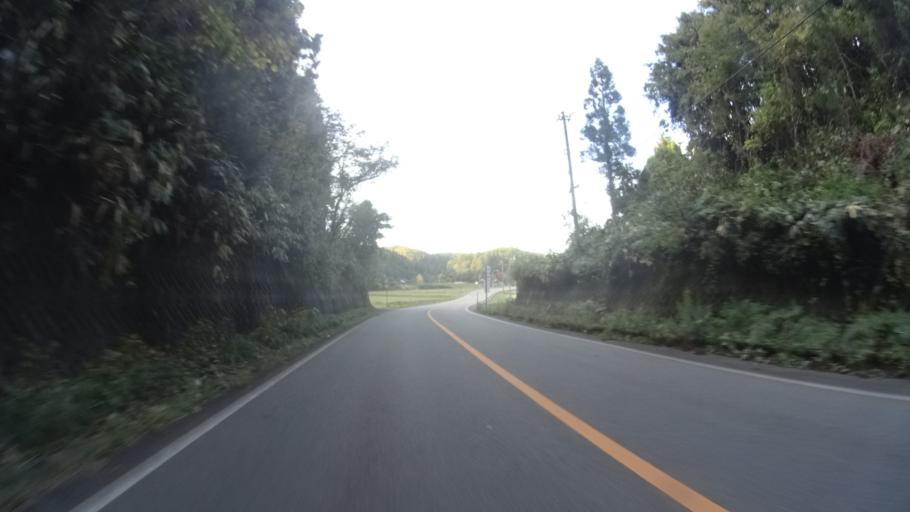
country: JP
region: Ishikawa
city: Nanao
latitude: 37.1836
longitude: 136.7142
